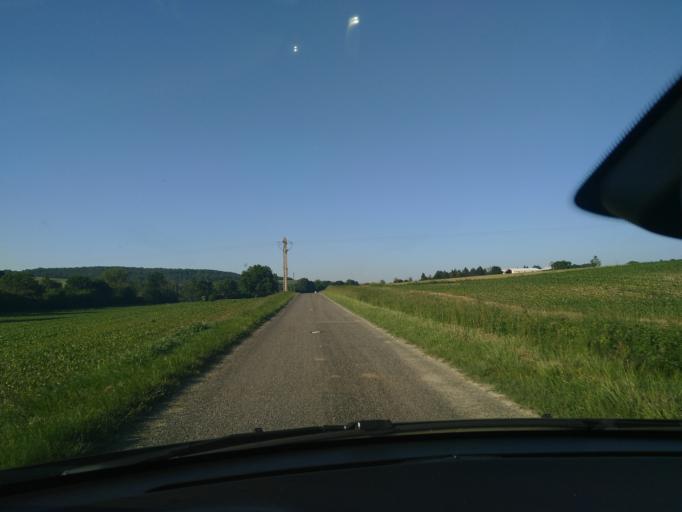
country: FR
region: Midi-Pyrenees
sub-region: Departement du Tarn-et-Garonne
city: Beaumont-de-Lomagne
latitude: 43.8376
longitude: 1.0705
